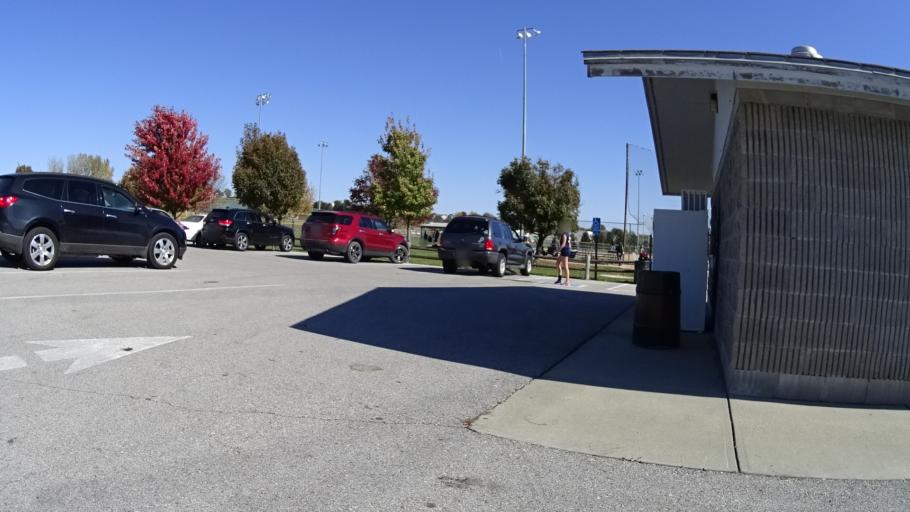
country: US
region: Nebraska
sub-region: Sarpy County
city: Papillion
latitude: 41.1552
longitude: -96.0277
